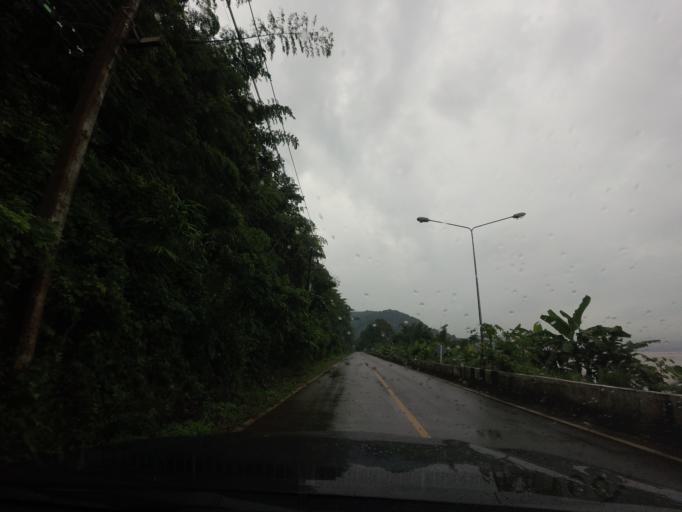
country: TH
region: Nong Khai
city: Sangkhom
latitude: 18.2074
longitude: 102.1247
